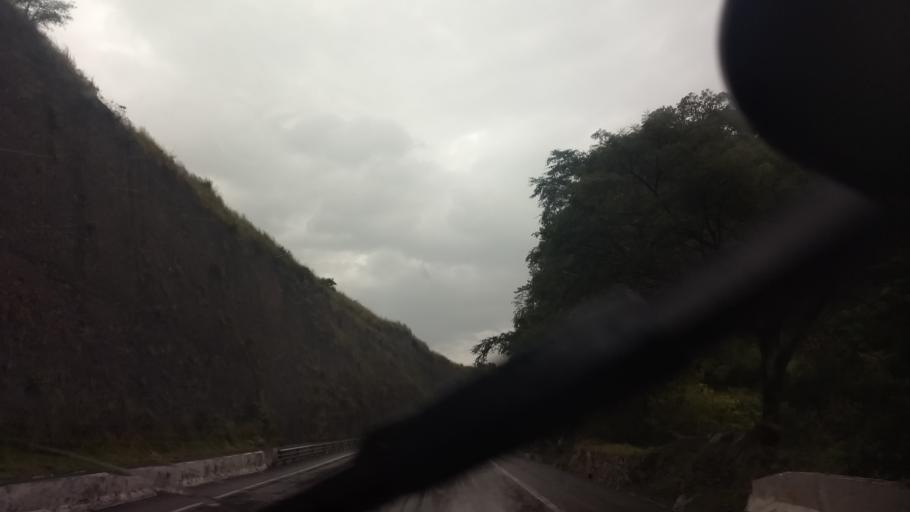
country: MX
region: Jalisco
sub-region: Tonila
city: San Marcos
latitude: 19.4480
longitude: -103.4741
